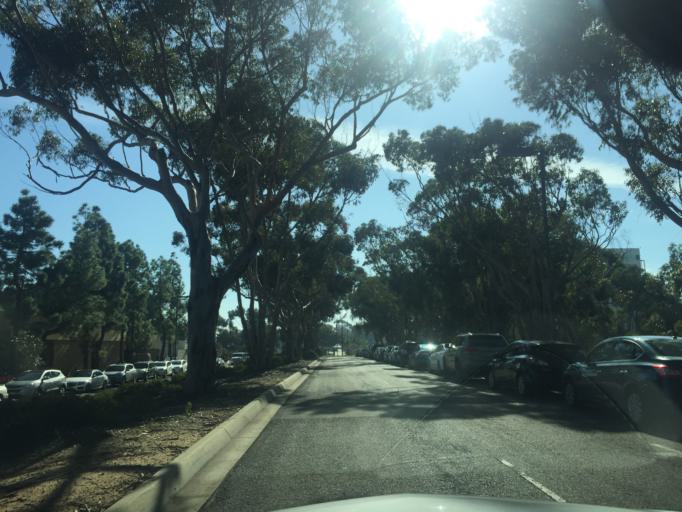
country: US
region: California
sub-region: San Diego County
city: La Jolla
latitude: 32.8904
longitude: -117.2409
